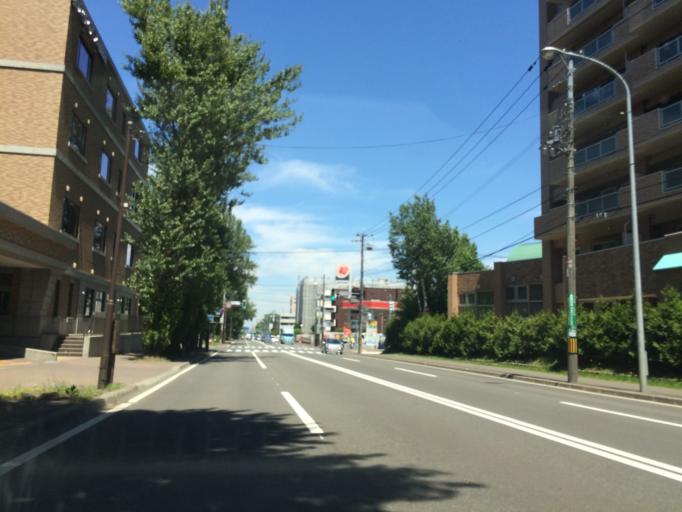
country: JP
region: Hokkaido
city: Sapporo
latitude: 42.9938
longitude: 141.3495
